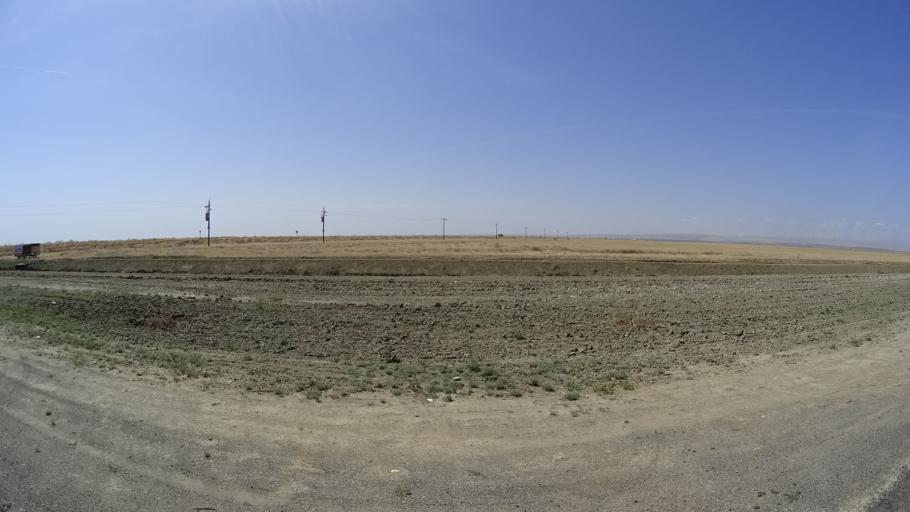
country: US
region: California
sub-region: Kings County
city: Kettleman City
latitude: 36.0941
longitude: -119.9118
